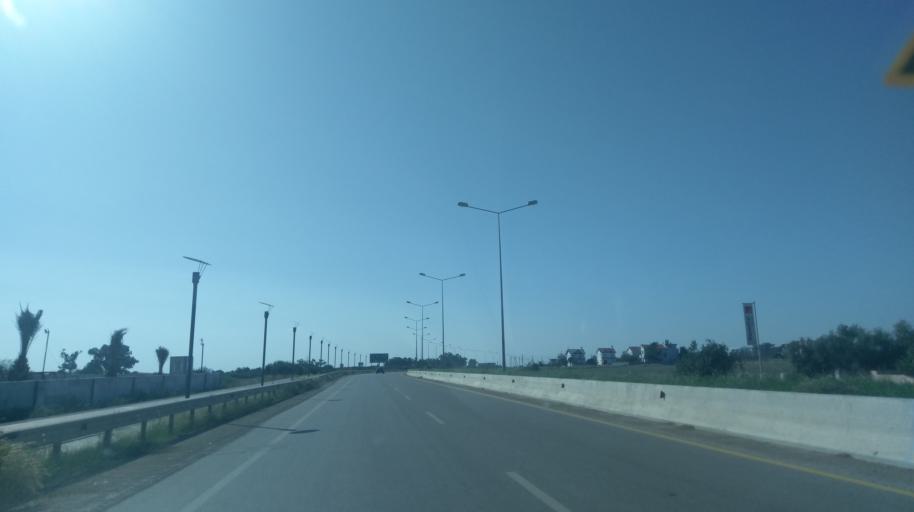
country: CY
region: Ammochostos
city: Trikomo
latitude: 35.2666
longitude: 33.9134
